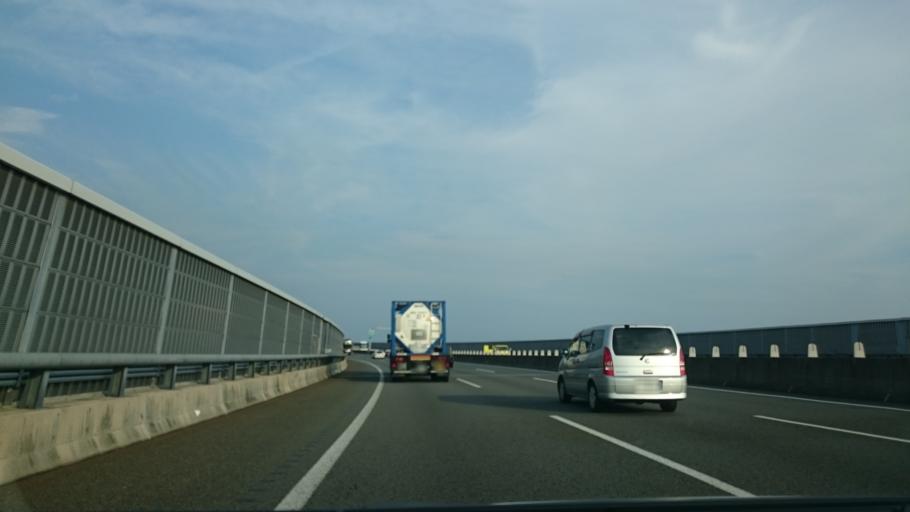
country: JP
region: Mie
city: Yokkaichi
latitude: 35.0287
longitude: 136.6468
